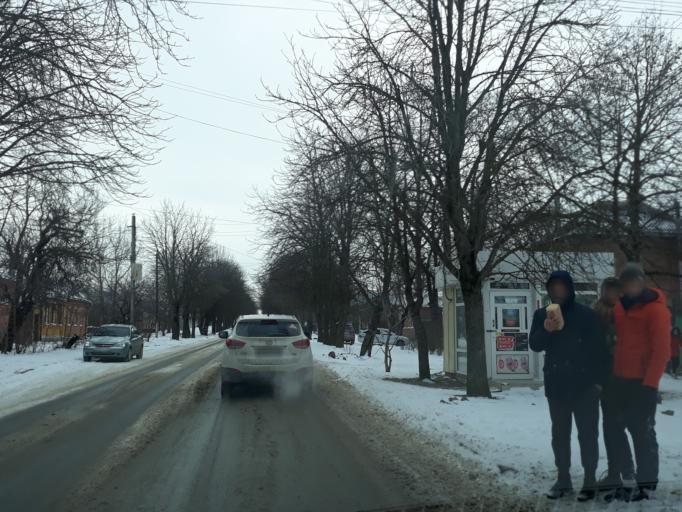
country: RU
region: Rostov
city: Taganrog
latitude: 47.2058
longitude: 38.9207
